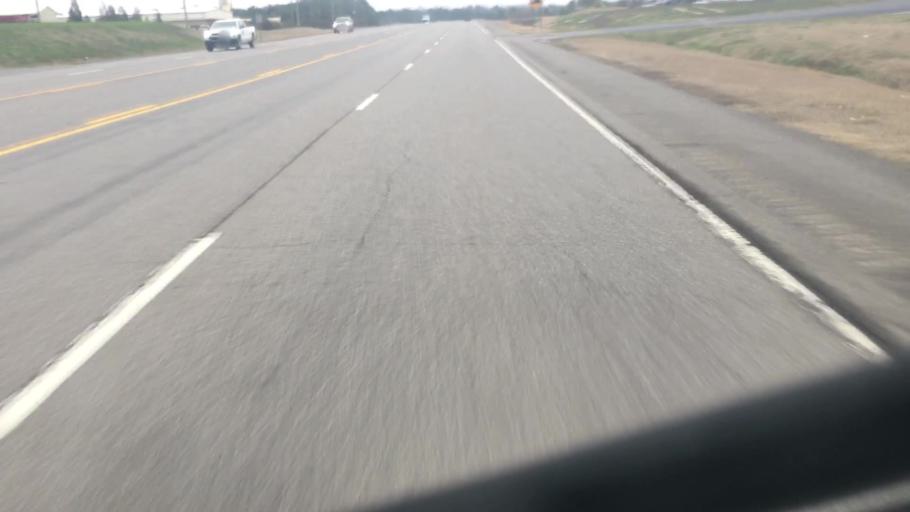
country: US
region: Alabama
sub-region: Walker County
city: Jasper
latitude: 33.8103
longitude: -87.2339
